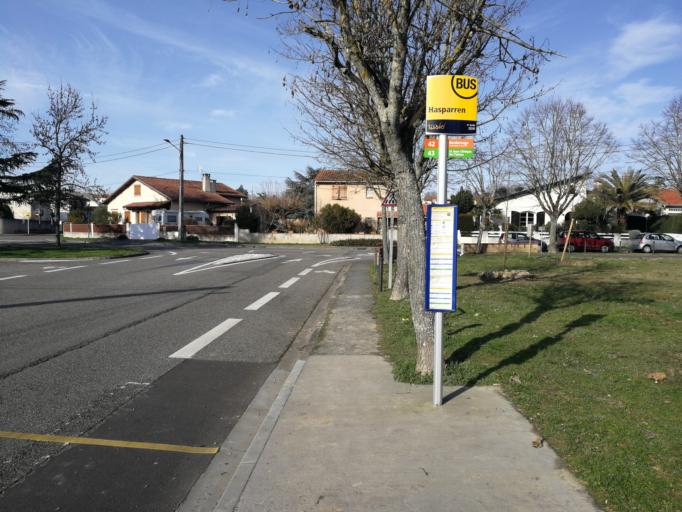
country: FR
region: Midi-Pyrenees
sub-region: Departement de la Haute-Garonne
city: L'Union
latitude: 43.6502
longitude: 1.4842
